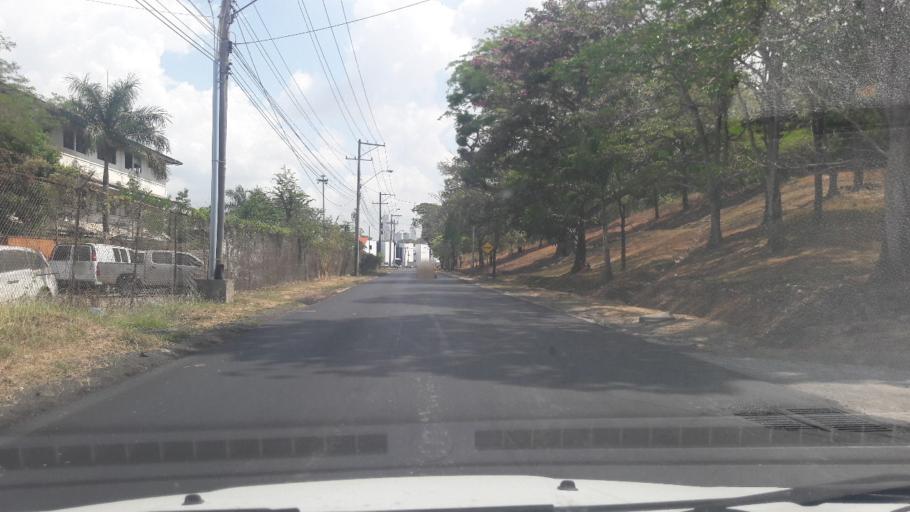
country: PA
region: Panama
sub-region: Distrito de Panama
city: Ancon
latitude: 8.9733
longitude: -79.5463
